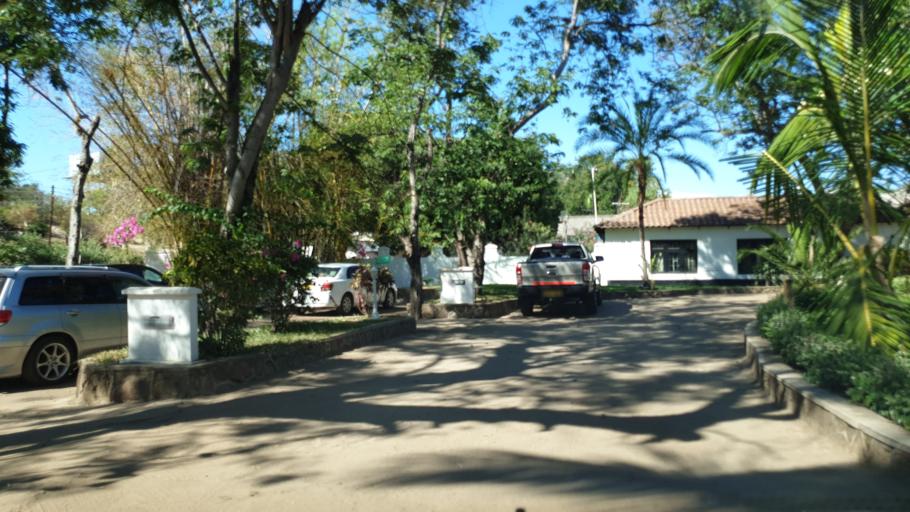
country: MW
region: Central Region
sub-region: Salima District
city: Salima
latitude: -13.7187
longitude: 34.6264
